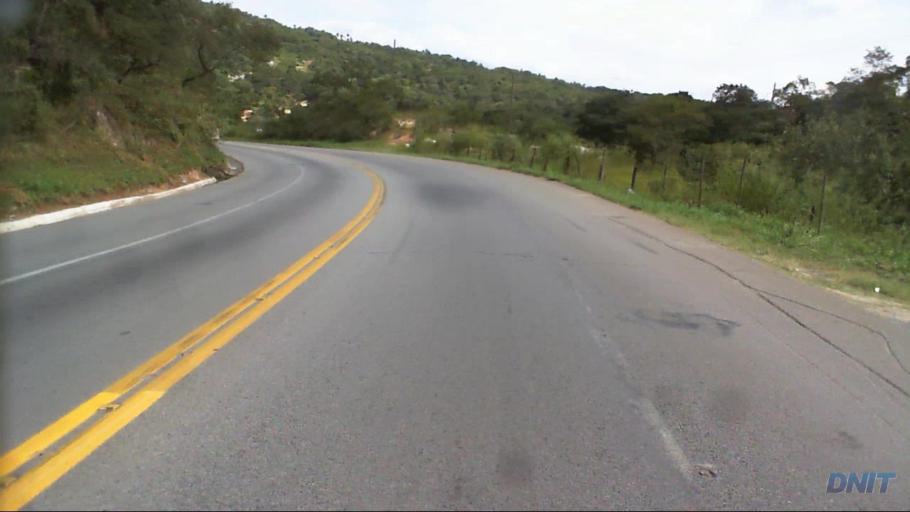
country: BR
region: Minas Gerais
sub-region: Santa Luzia
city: Santa Luzia
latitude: -19.8183
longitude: -43.8114
